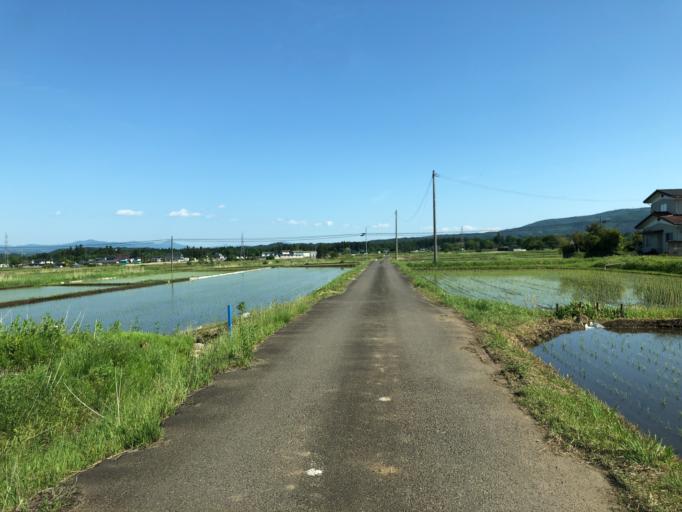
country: JP
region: Fukushima
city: Fukushima-shi
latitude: 37.7451
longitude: 140.3760
